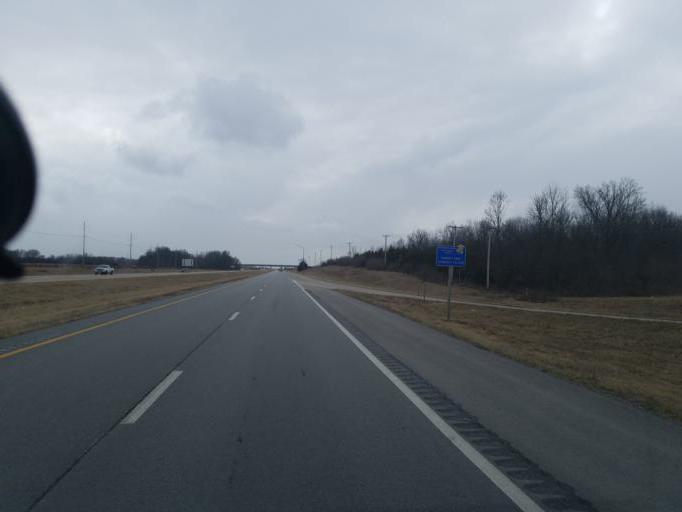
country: US
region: Missouri
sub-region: Randolph County
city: Moberly
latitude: 39.4156
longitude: -92.4123
